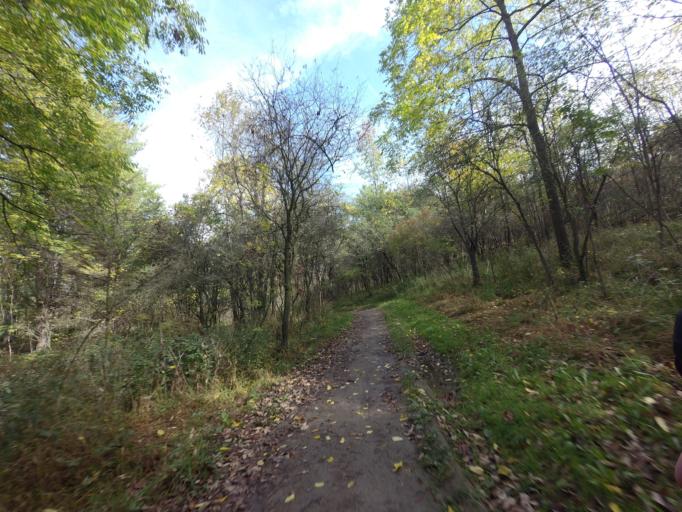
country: CA
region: Ontario
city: Ancaster
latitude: 43.2514
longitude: -79.9804
